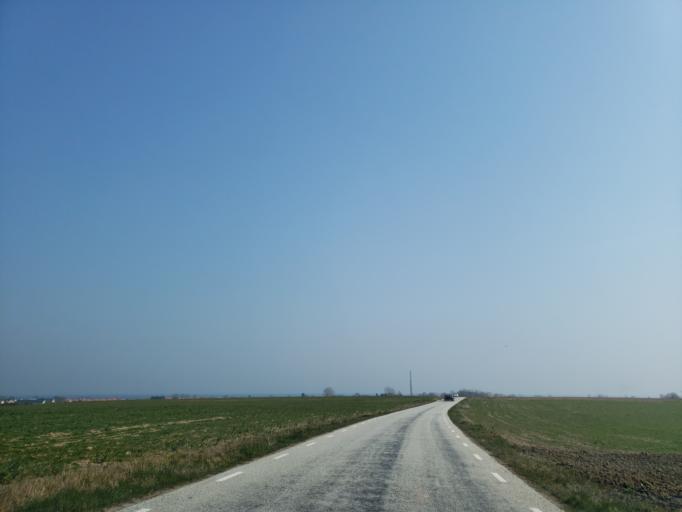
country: SE
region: Skane
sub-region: Simrishamns Kommun
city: Simrishamn
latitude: 55.5112
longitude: 14.3281
